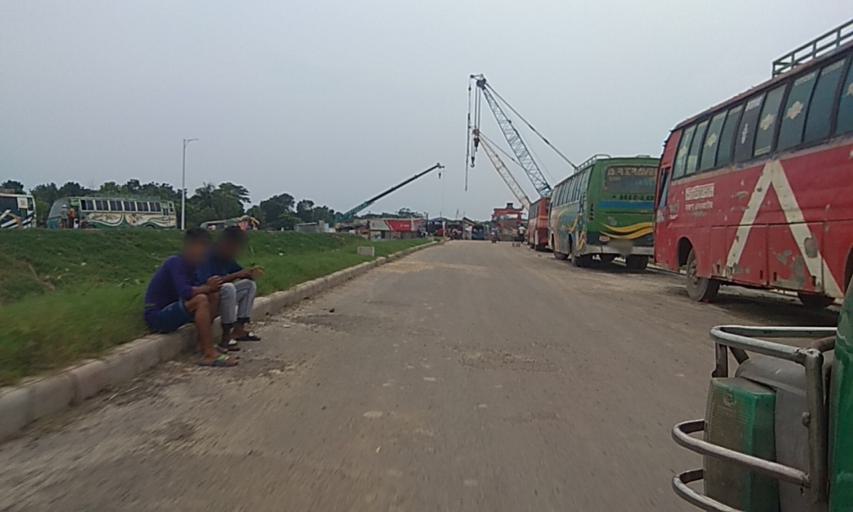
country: BD
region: Dhaka
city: Char Bhadrasan
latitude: 23.3885
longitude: 89.9840
